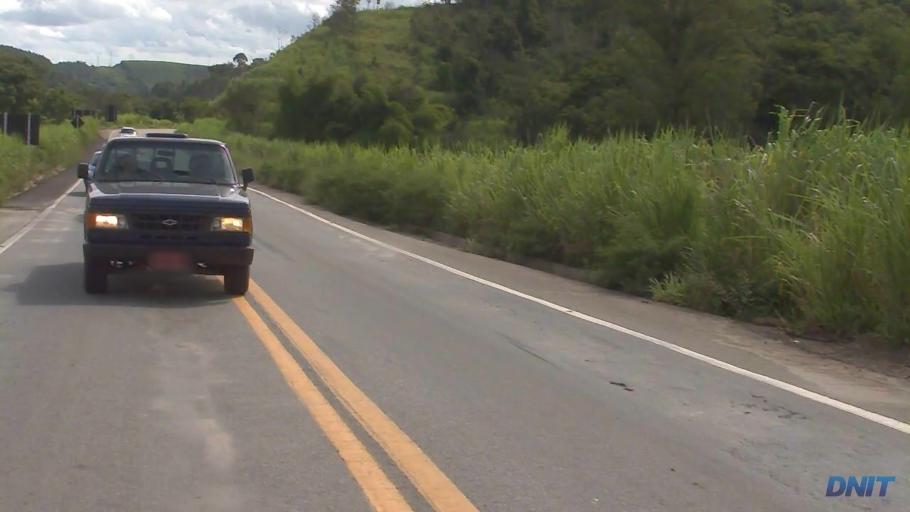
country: BR
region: Minas Gerais
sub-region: Ipaba
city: Ipaba
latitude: -19.3858
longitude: -42.4754
